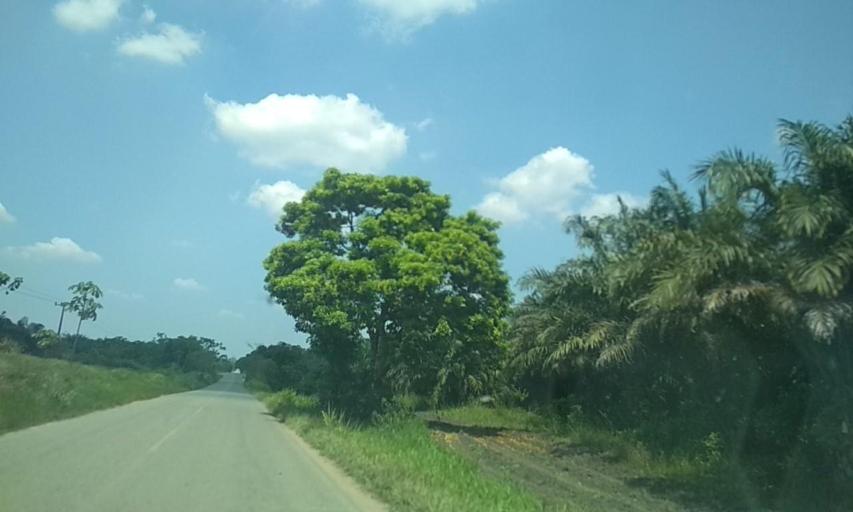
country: MX
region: Tabasco
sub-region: Huimanguillo
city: Paso de la Mina 2da. Seccion (Barrial)
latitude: 17.7595
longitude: -93.6574
